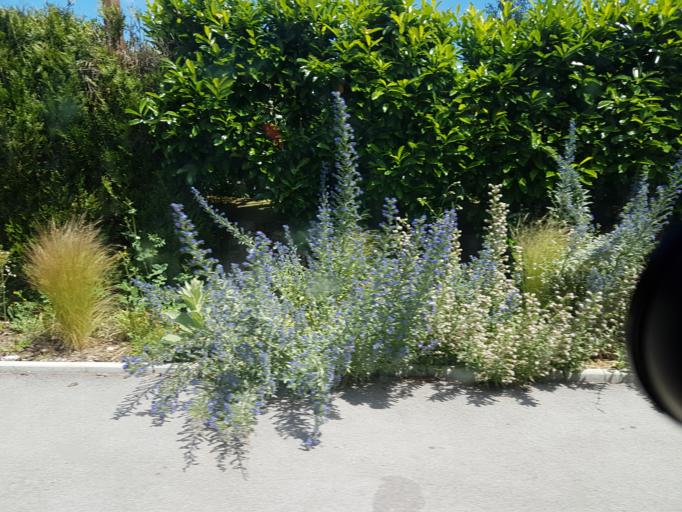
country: FR
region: Bourgogne
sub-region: Departement de Saone-et-Loire
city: Curgy
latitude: 47.0461
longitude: 4.3771
